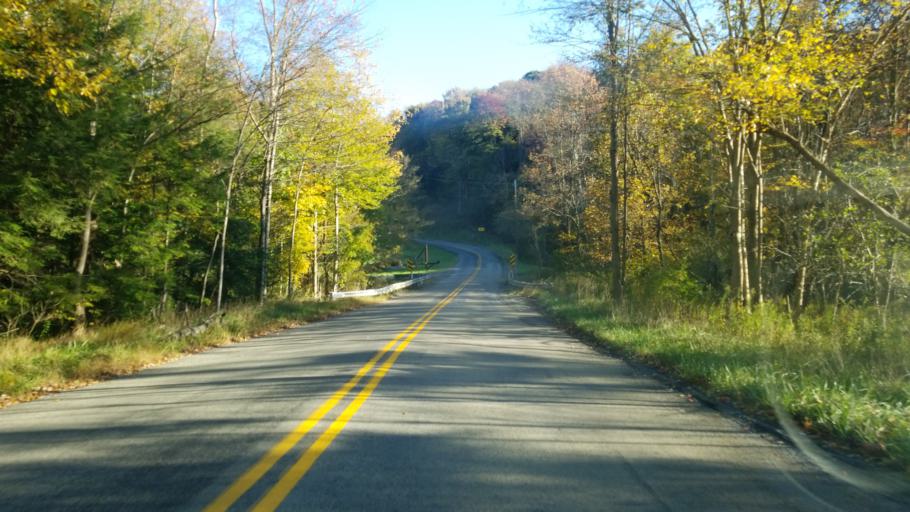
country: US
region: Pennsylvania
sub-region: Indiana County
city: Johnsonburg
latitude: 40.9140
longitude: -78.8814
